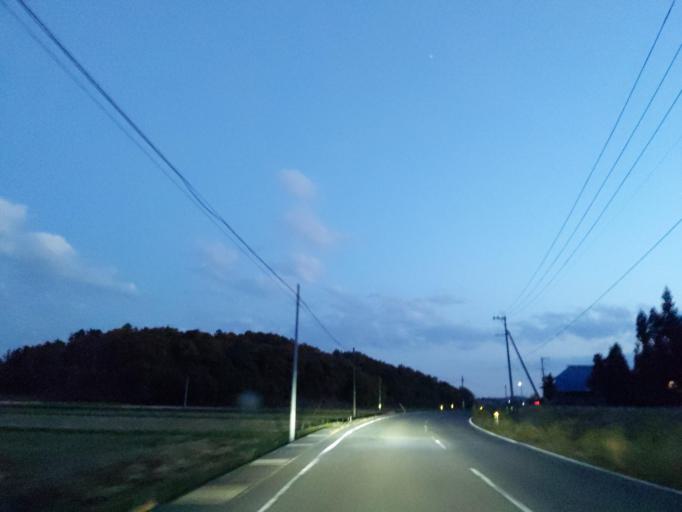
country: JP
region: Fukushima
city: Koriyama
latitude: 37.4401
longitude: 140.3114
